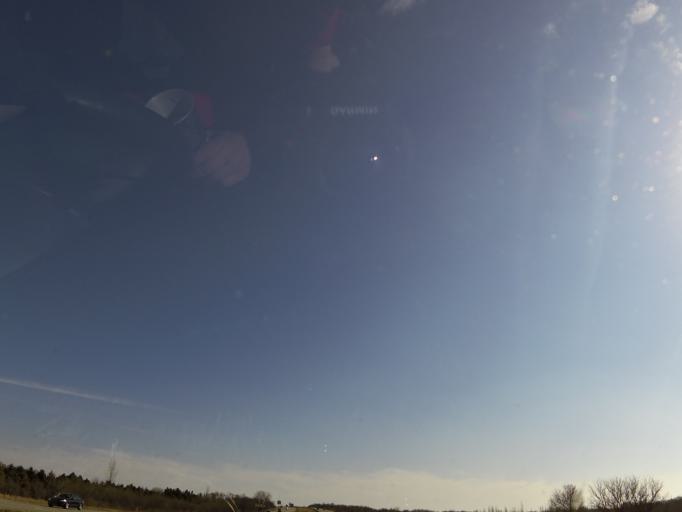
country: US
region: Minnesota
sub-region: Steele County
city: Owatonna
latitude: 44.0478
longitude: -93.2496
